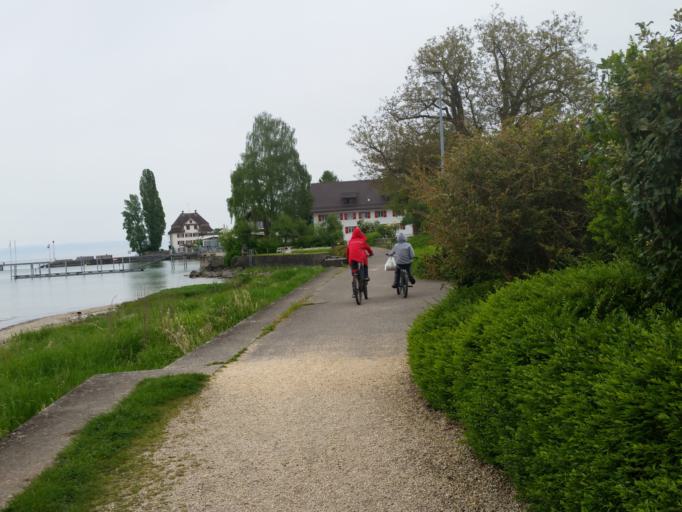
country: CH
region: Thurgau
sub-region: Arbon District
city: Uttwil
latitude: 47.5867
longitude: 9.3413
